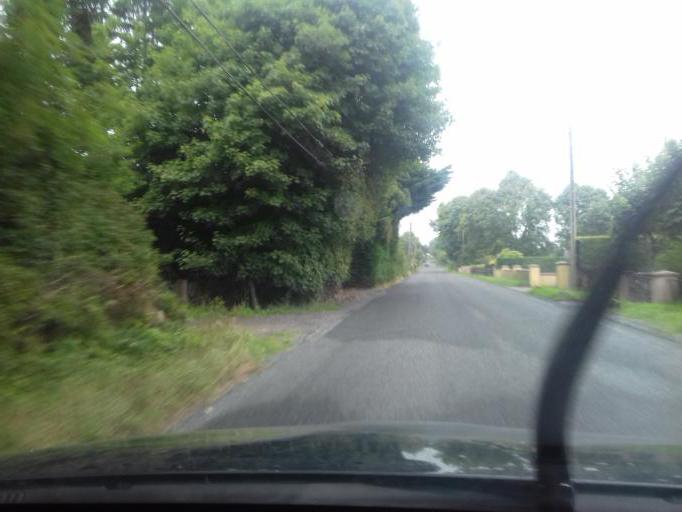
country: IE
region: Leinster
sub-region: Kilkenny
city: Graiguenamanagh
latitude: 52.6098
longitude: -6.9369
